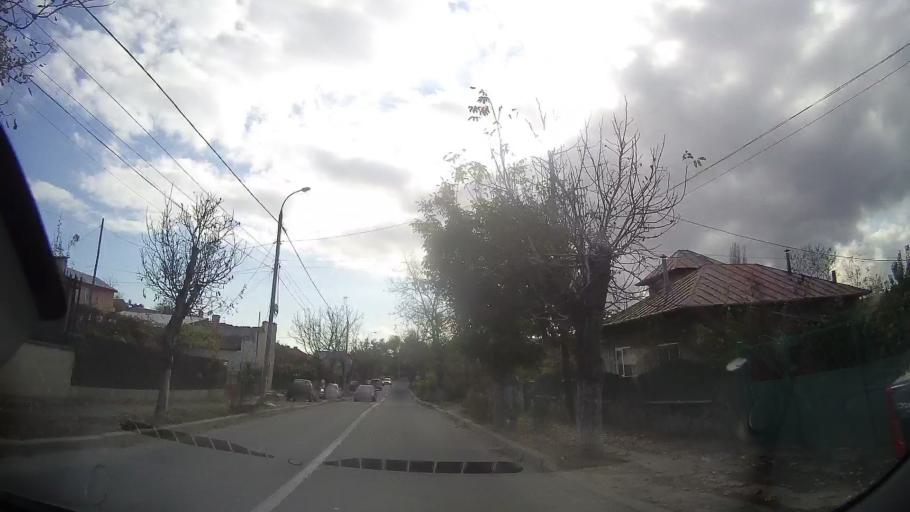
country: RO
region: Constanta
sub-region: Oras Techirghiol
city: Techirghiol
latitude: 44.0567
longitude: 28.6004
